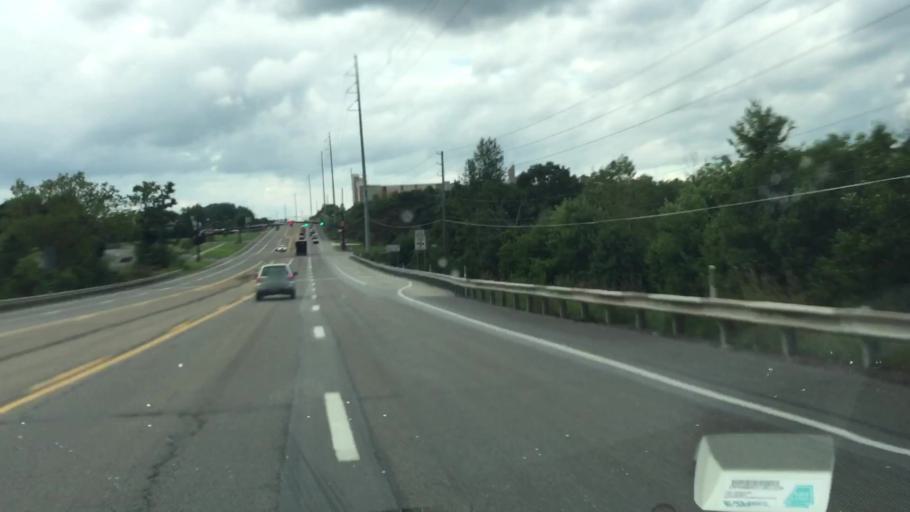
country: US
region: Pennsylvania
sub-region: Butler County
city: Fox Run
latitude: 40.7329
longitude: -80.1093
